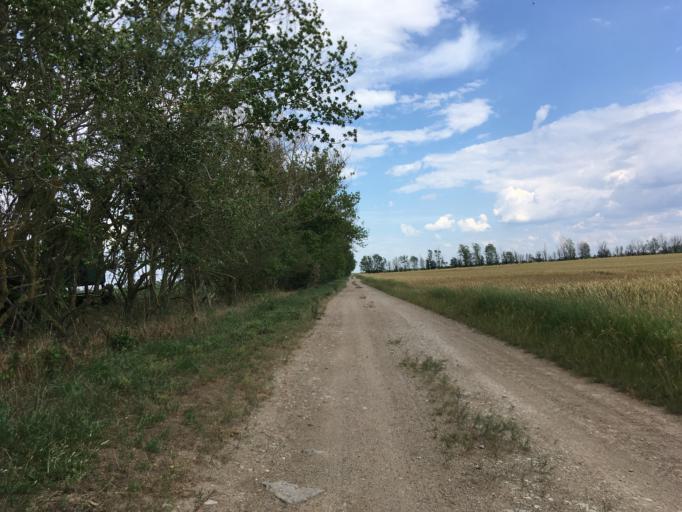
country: DE
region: Saxony-Anhalt
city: Wulfen
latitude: 51.7610
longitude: 11.8858
